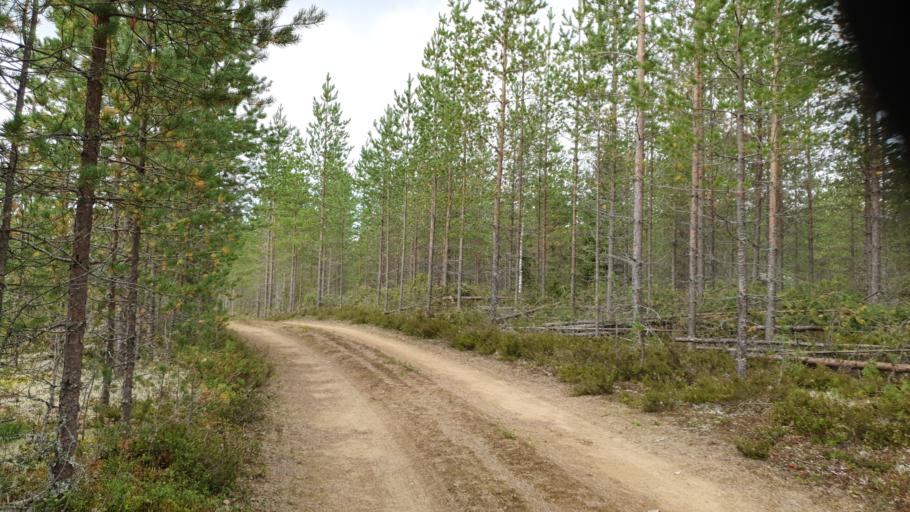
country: FI
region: Kainuu
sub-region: Kehys-Kainuu
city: Kuhmo
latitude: 64.1499
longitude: 29.3974
